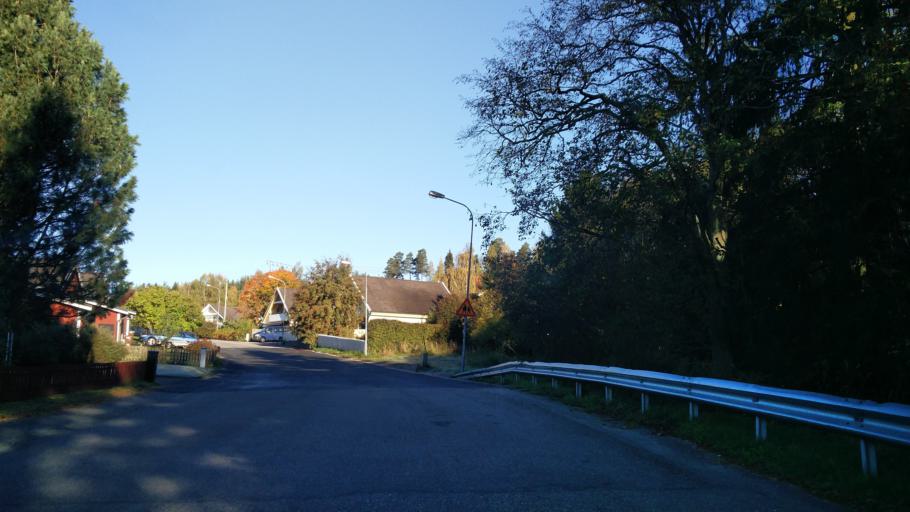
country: SE
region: Vaesternorrland
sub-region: Sundsvalls Kommun
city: Sundsvall
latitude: 62.4055
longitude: 17.2654
